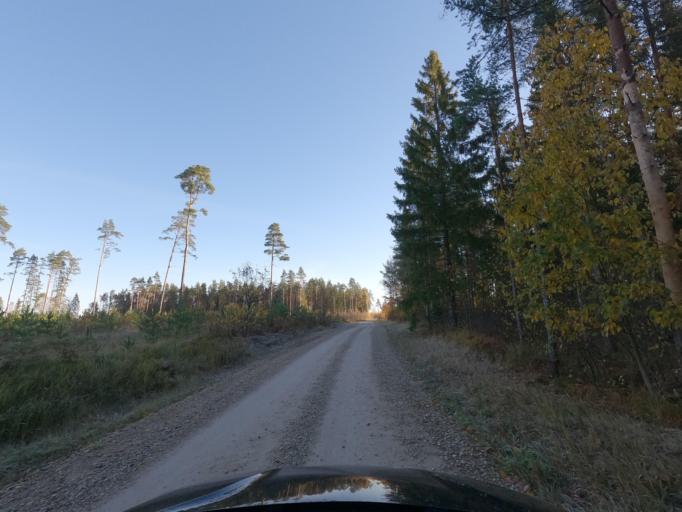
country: EE
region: Raplamaa
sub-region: Kohila vald
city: Kohila
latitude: 59.1246
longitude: 24.7700
